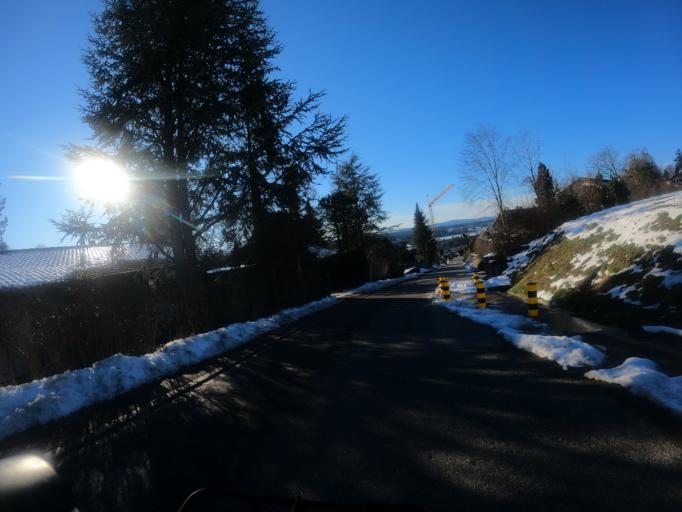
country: CH
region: Aargau
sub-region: Bezirk Bremgarten
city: Unterlunkhofen
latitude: 47.3231
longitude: 8.3871
